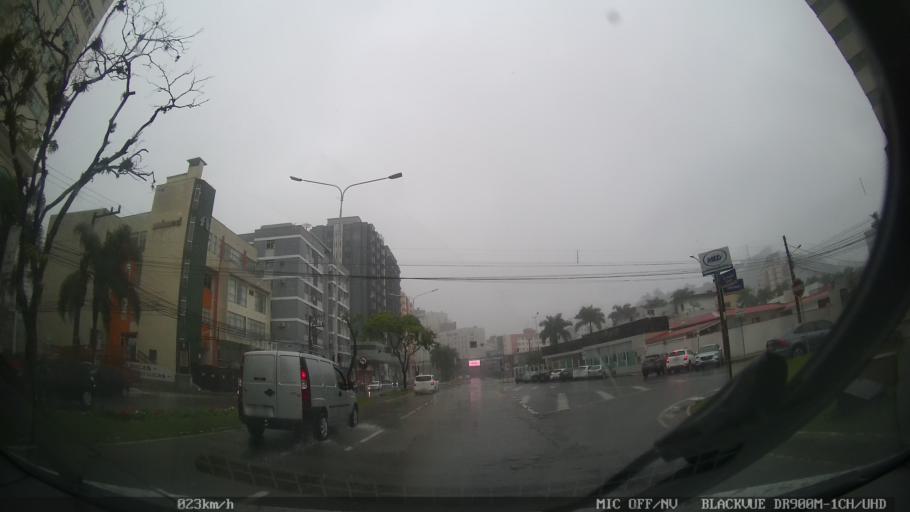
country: BR
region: Santa Catarina
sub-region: Itajai
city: Itajai
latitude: -26.9118
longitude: -48.6597
